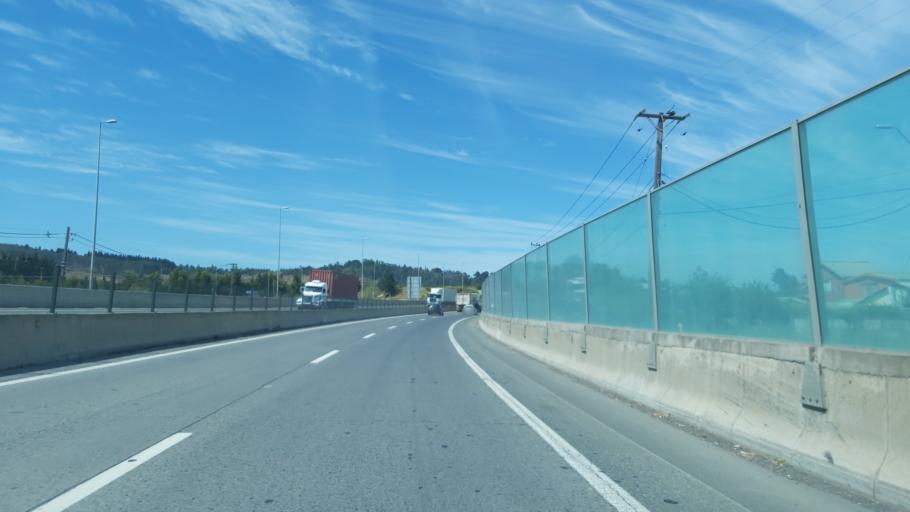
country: CL
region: Biobio
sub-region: Provincia de Concepcion
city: Coronel
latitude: -37.0387
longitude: -73.1350
